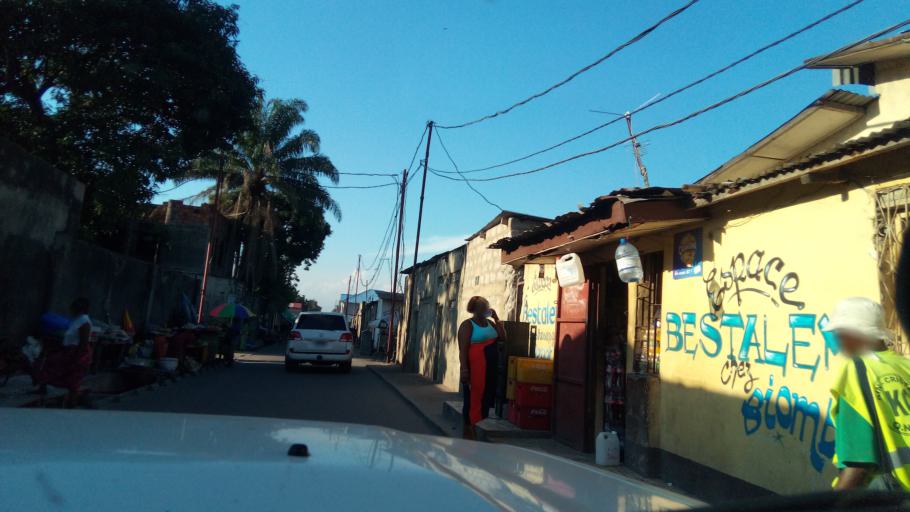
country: CD
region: Kinshasa
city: Kinshasa
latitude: -4.3443
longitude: 15.2687
